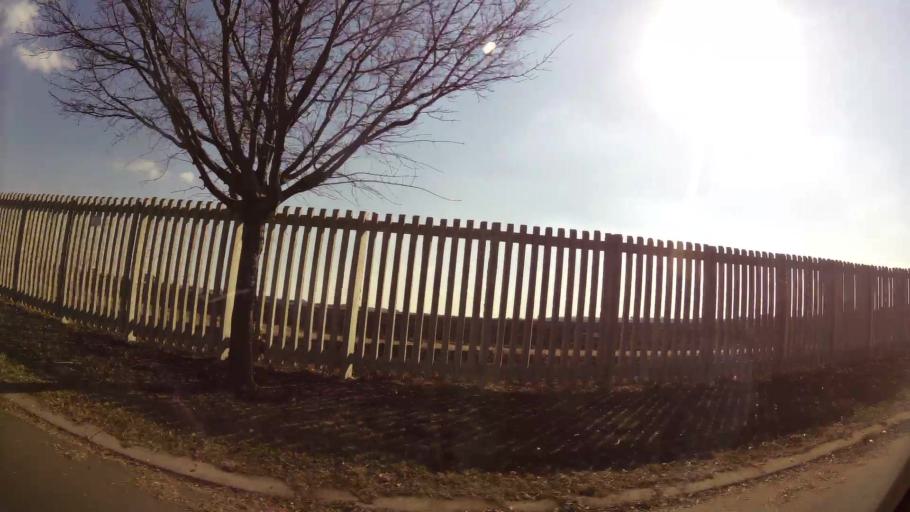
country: ZA
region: Gauteng
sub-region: Ekurhuleni Metropolitan Municipality
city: Benoni
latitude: -26.2406
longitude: 28.3073
